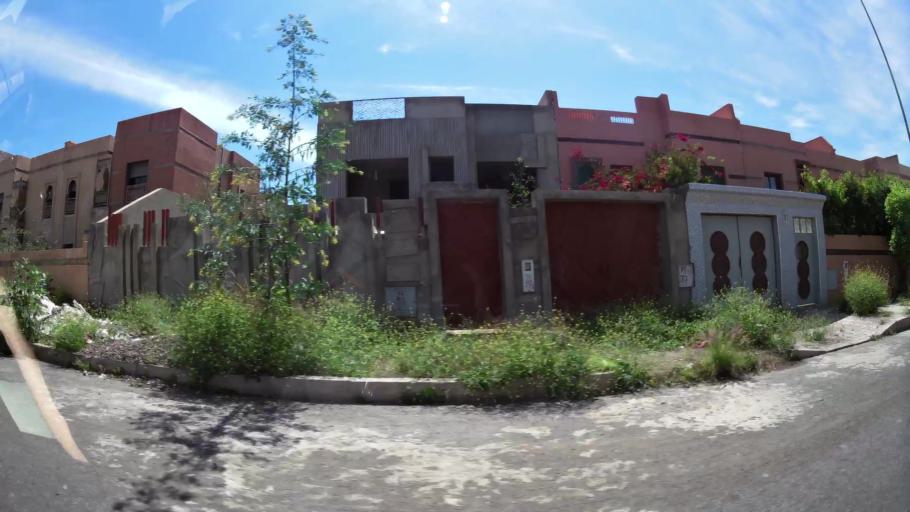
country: MA
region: Marrakech-Tensift-Al Haouz
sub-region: Marrakech
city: Marrakesh
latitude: 31.6506
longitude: -8.0714
